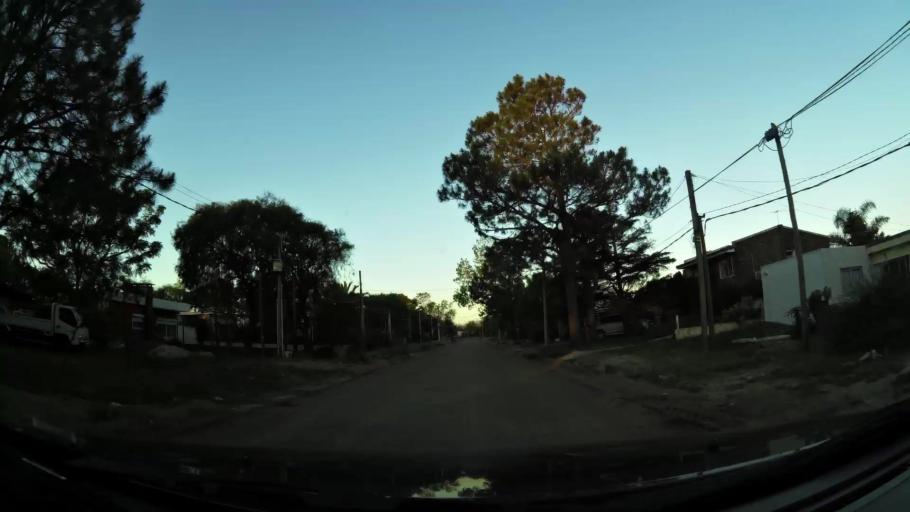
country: UY
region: Canelones
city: Barra de Carrasco
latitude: -34.8454
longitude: -55.9793
